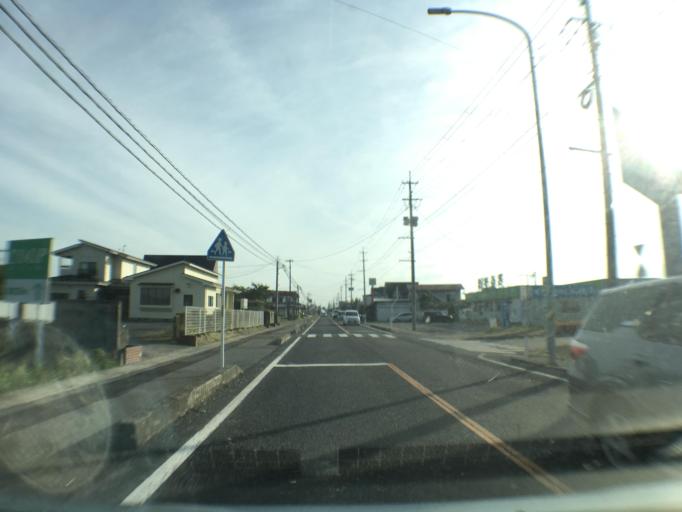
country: JP
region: Miyagi
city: Wakuya
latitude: 38.7127
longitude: 141.2408
